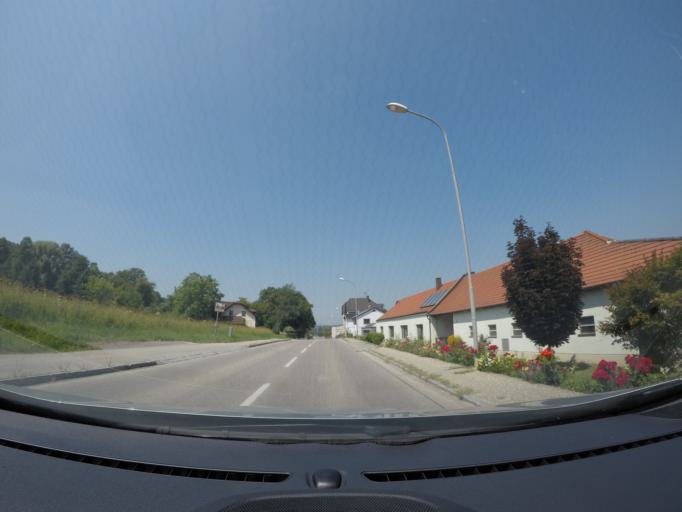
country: AT
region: Lower Austria
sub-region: Politischer Bezirk Sankt Polten
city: Maria-Anzbach
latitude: 48.1842
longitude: 15.9577
